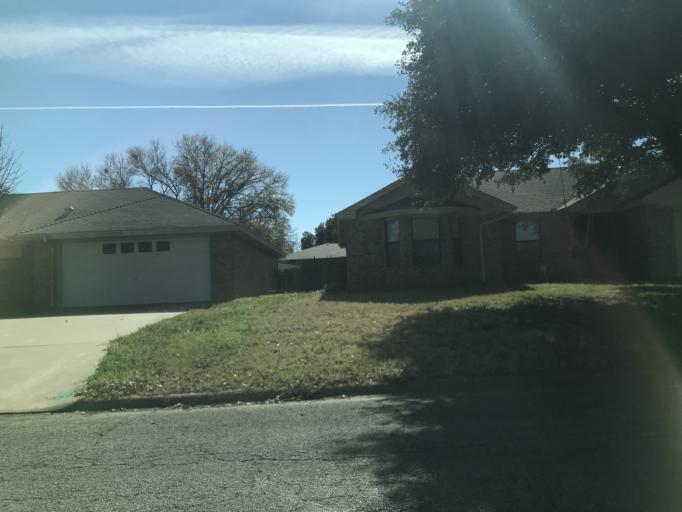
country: US
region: Texas
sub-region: Tom Green County
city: San Angelo
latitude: 31.4354
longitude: -100.4901
